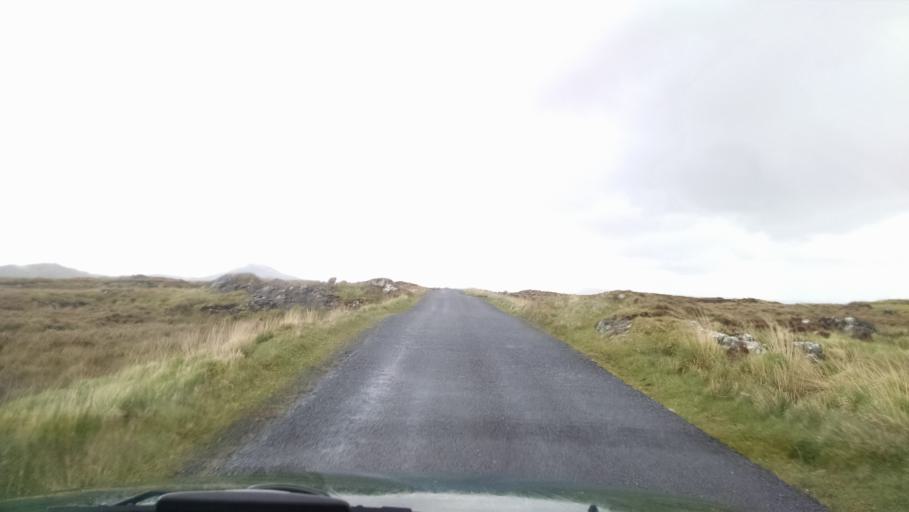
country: IE
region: Connaught
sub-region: County Galway
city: Clifden
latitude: 53.4373
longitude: -9.9142
